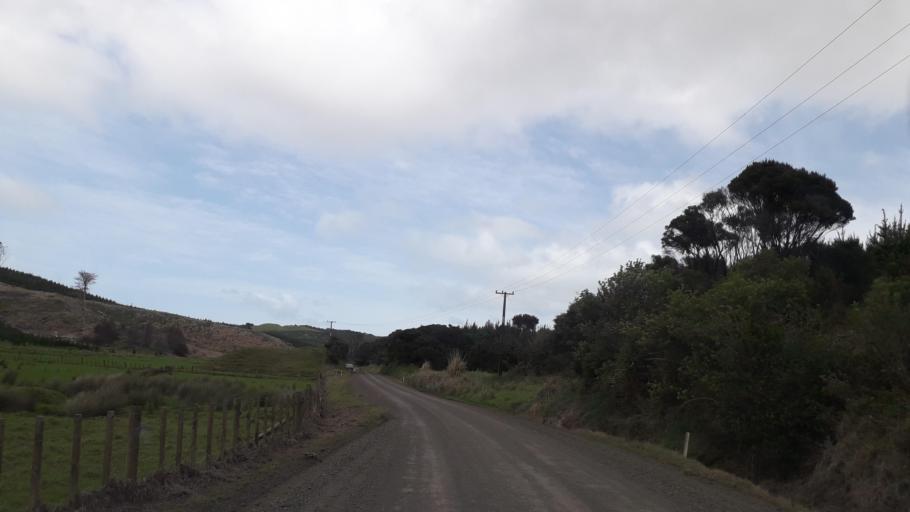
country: NZ
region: Northland
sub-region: Far North District
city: Ahipara
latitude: -35.4283
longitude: 173.3527
